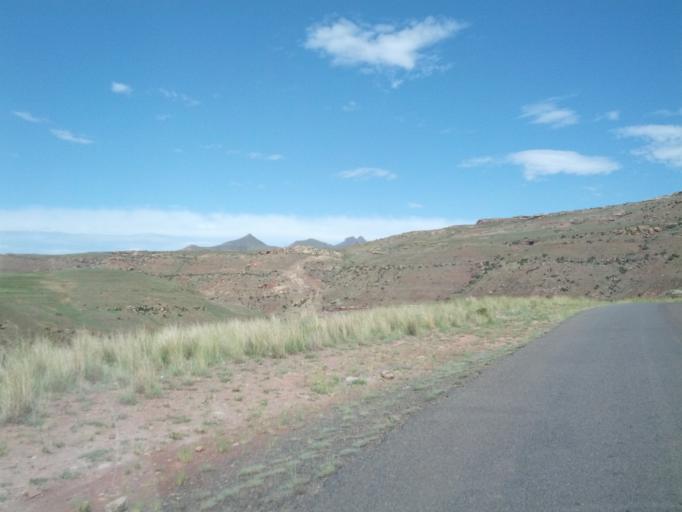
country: LS
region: Qacha's Nek
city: Qacha's Nek
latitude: -30.0678
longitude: 28.4608
